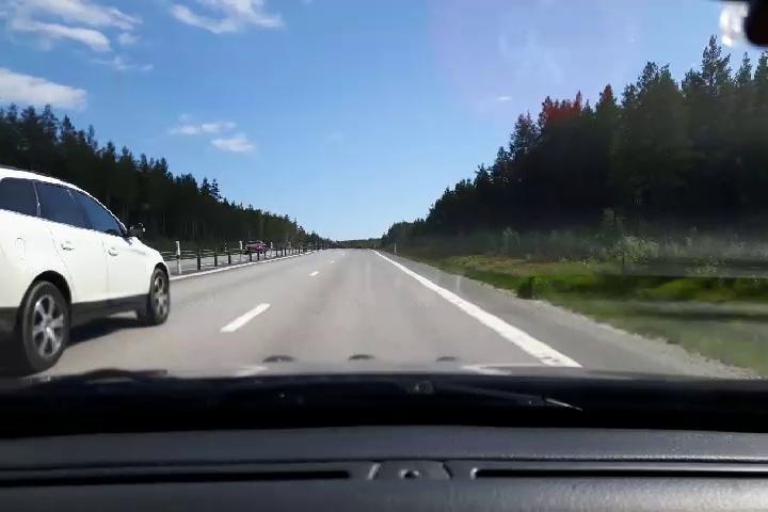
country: SE
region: Gaevleborg
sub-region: Hudiksvalls Kommun
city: Hudiksvall
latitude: 61.7057
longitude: 17.0512
